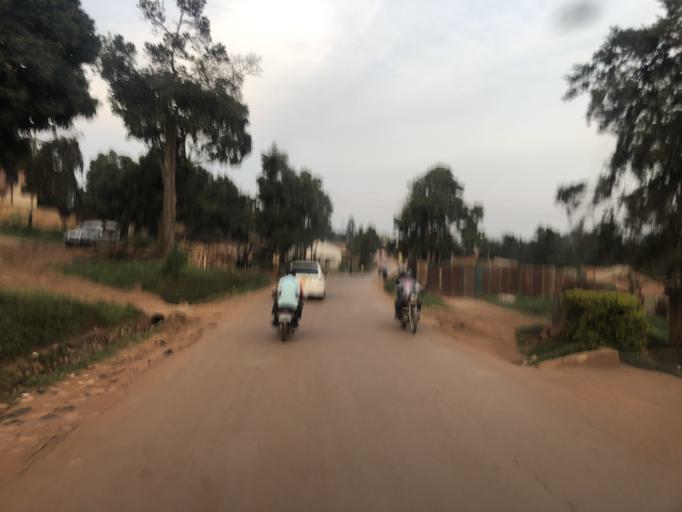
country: UG
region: Central Region
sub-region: Kampala District
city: Kampala
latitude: 0.2731
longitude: 32.5481
